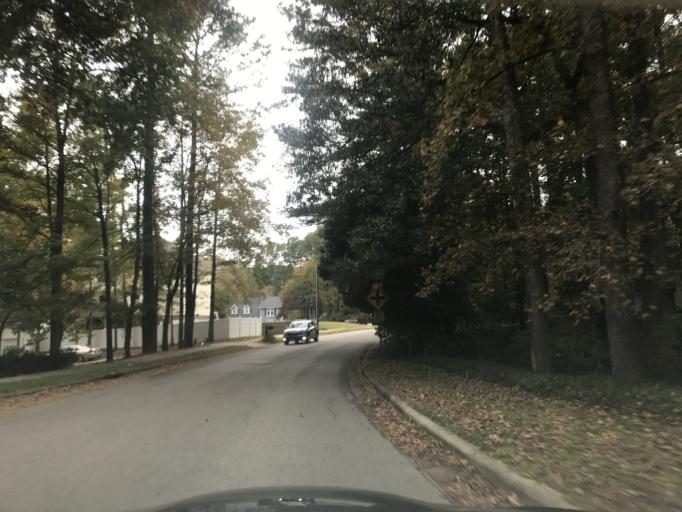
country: US
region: North Carolina
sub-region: Wake County
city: West Raleigh
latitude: 35.8906
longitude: -78.6329
